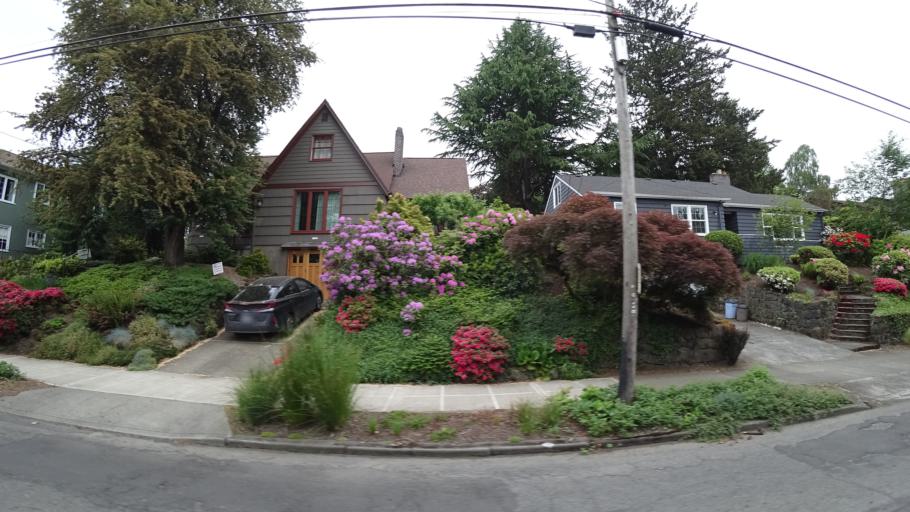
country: US
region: Oregon
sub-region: Multnomah County
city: Lents
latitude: 45.5149
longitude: -122.6020
